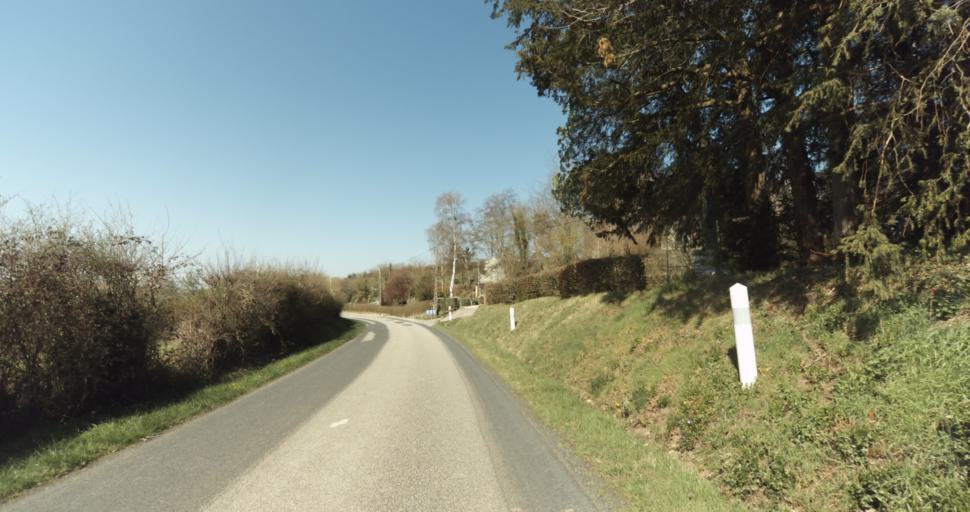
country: FR
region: Lower Normandy
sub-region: Departement du Calvados
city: Saint-Pierre-sur-Dives
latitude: 49.0152
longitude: -0.0214
